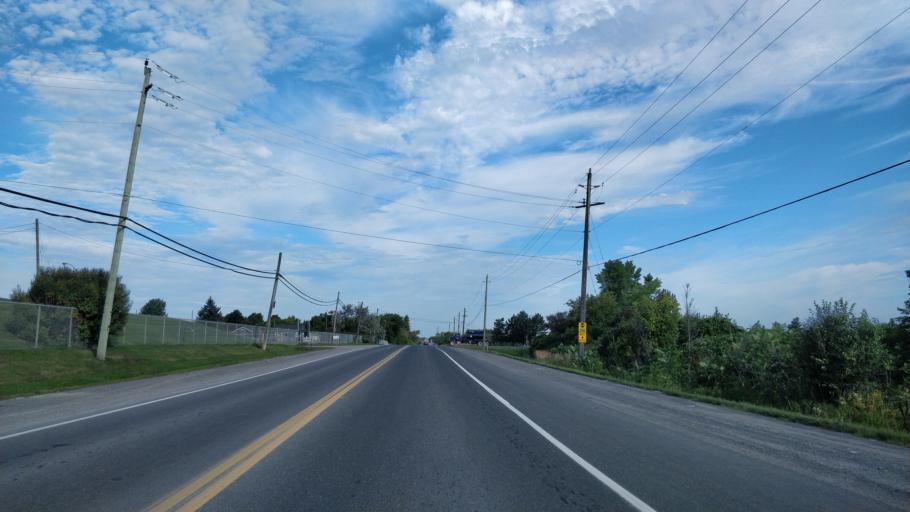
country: CA
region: Ontario
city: Bells Corners
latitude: 45.2843
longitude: -75.9611
